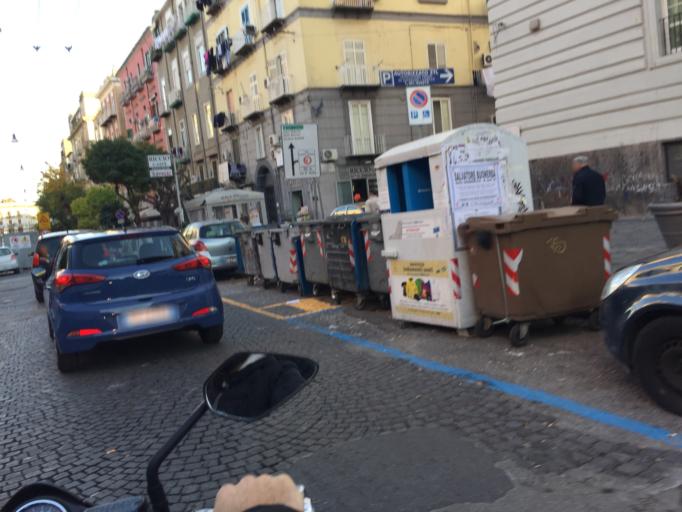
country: IT
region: Campania
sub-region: Provincia di Napoli
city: Napoli
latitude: 40.8550
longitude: 14.2619
